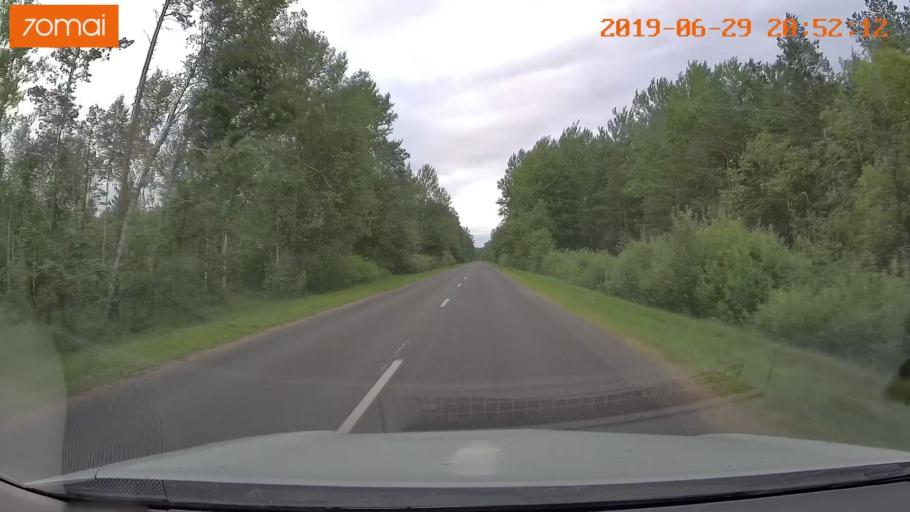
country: BY
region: Brest
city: Hantsavichy
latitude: 52.6968
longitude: 26.3597
